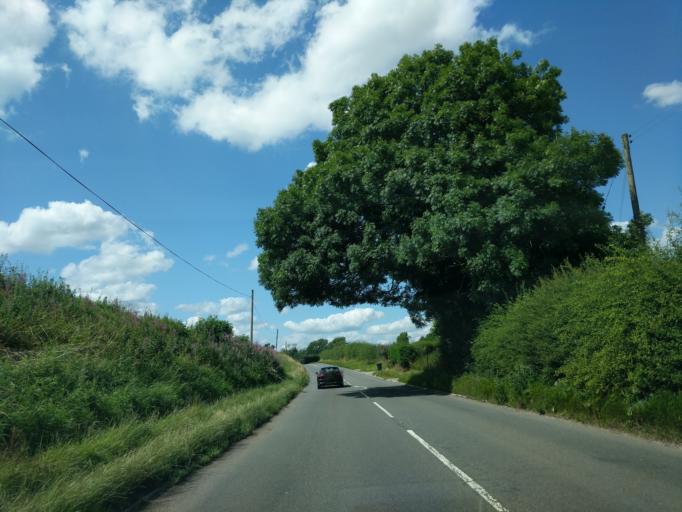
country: GB
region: England
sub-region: Staffordshire
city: Uttoxeter
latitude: 52.9272
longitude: -1.9178
